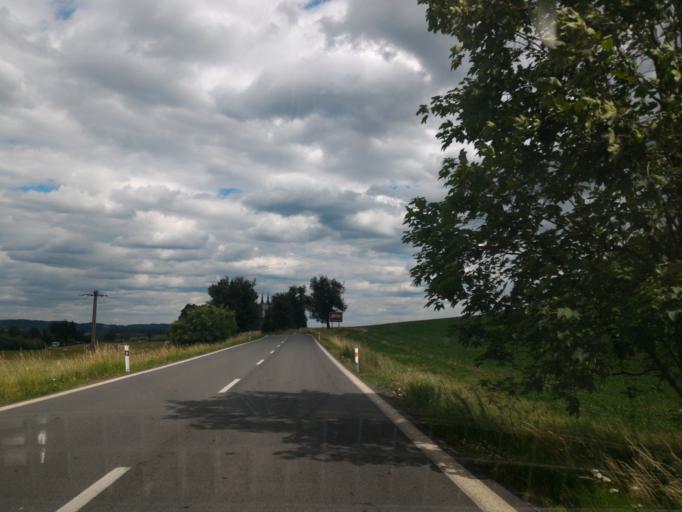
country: CZ
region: Vysocina
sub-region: Okres Jihlava
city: Telc
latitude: 49.1839
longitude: 15.4238
